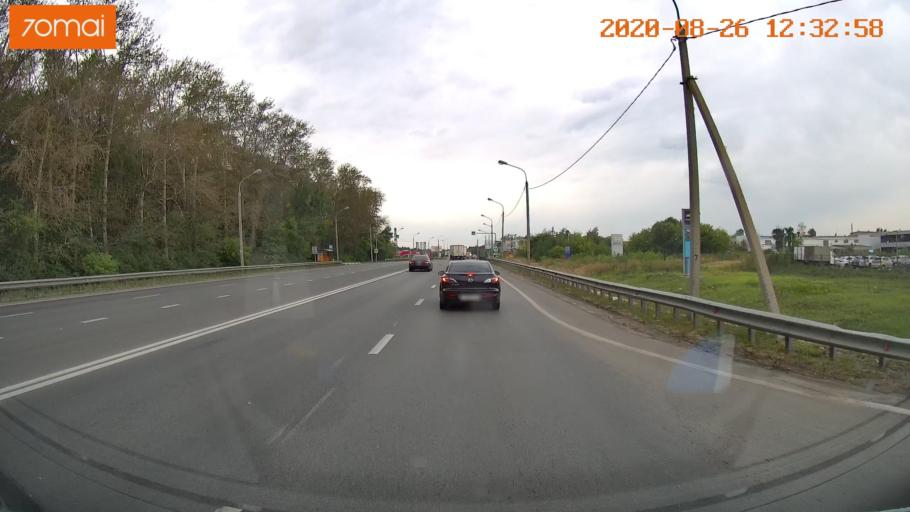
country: RU
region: Rjazan
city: Ryazan'
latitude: 54.5800
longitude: 39.7821
